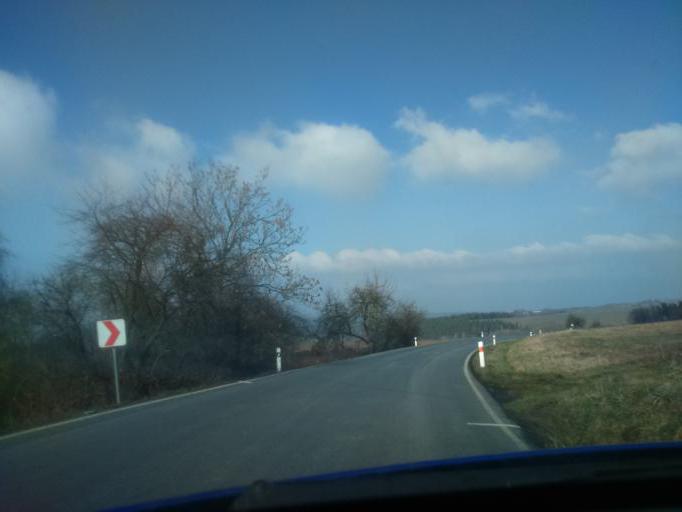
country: CZ
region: Plzensky
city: Horsovsky Tyn
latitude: 49.5007
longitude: 12.9460
